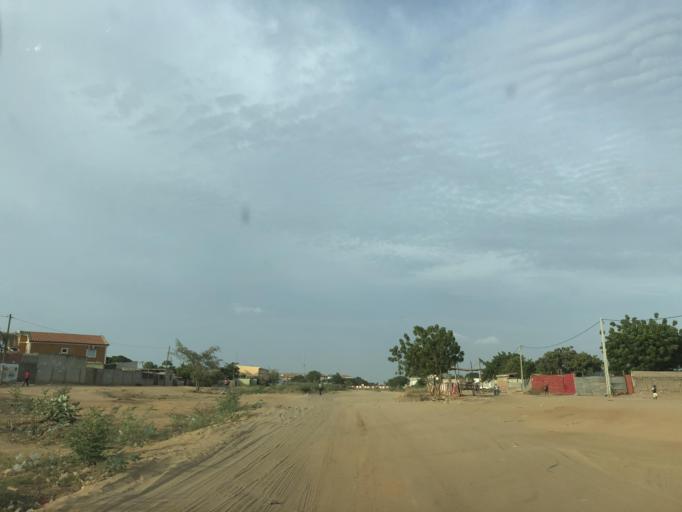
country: AO
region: Luanda
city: Luanda
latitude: -8.9168
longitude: 13.3110
